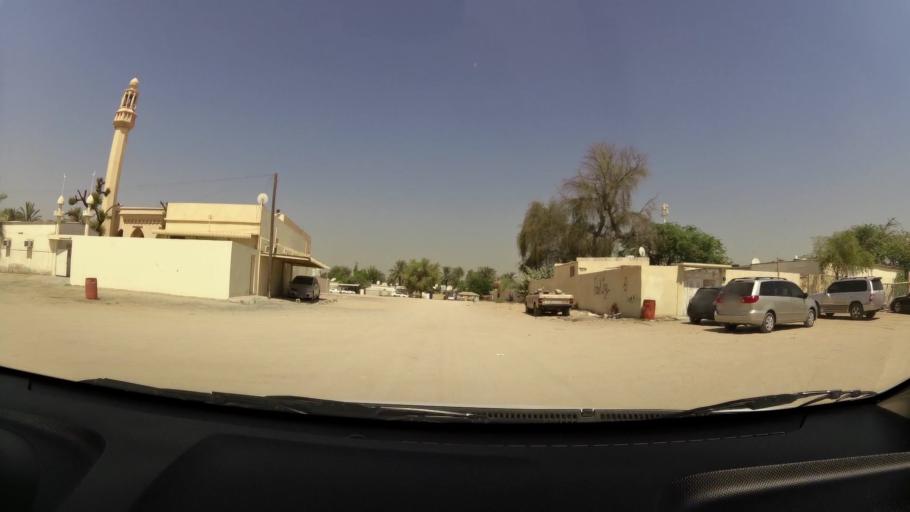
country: AE
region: Ajman
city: Ajman
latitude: 25.3965
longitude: 55.5295
